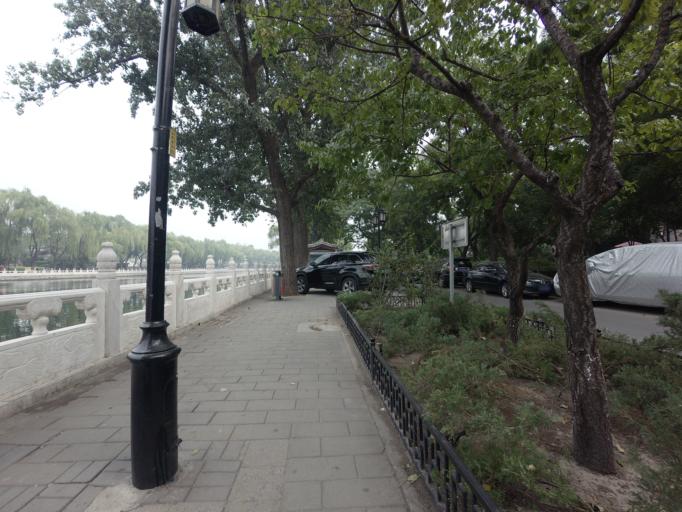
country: CN
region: Beijing
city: Jingshan
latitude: 39.9382
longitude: 116.3839
